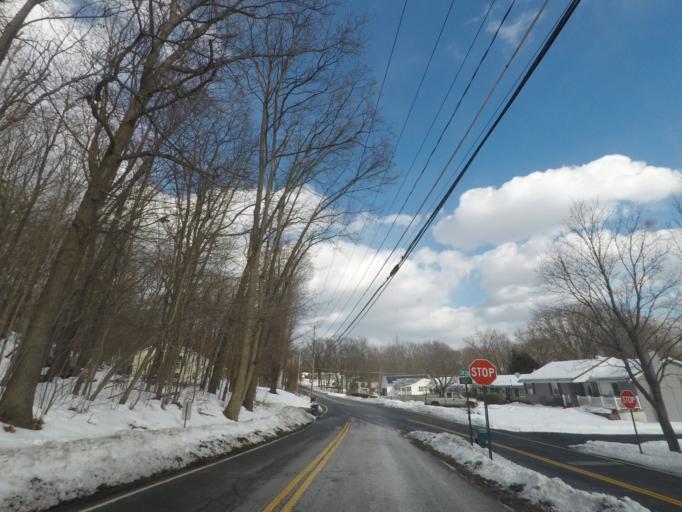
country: US
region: New York
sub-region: Albany County
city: Cohoes
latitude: 42.8106
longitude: -73.7515
